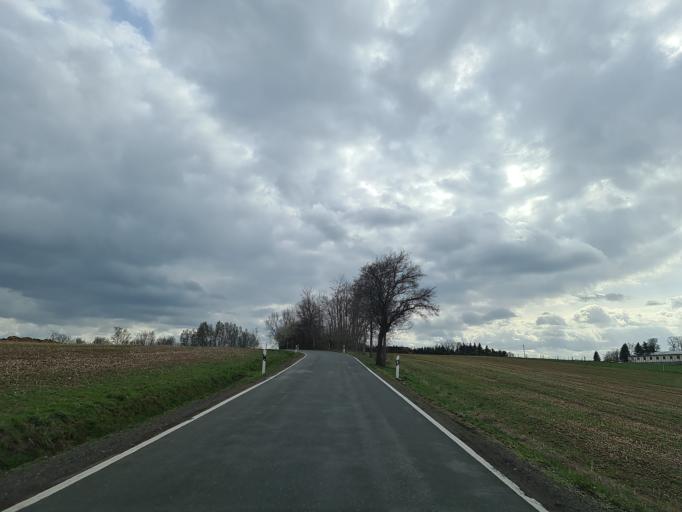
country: DE
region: Saxony
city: Wildenfels
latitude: 50.6911
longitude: 12.6093
